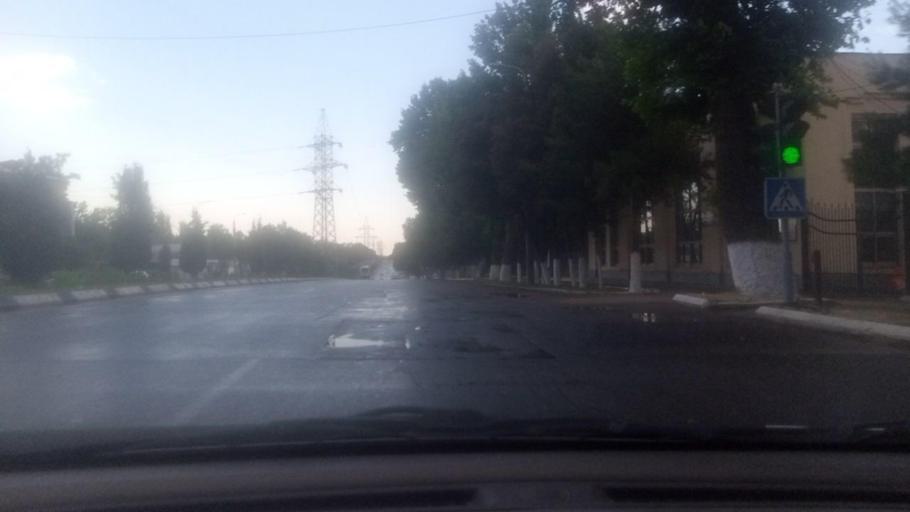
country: UZ
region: Toshkent Shahri
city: Tashkent
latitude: 41.3006
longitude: 69.1938
